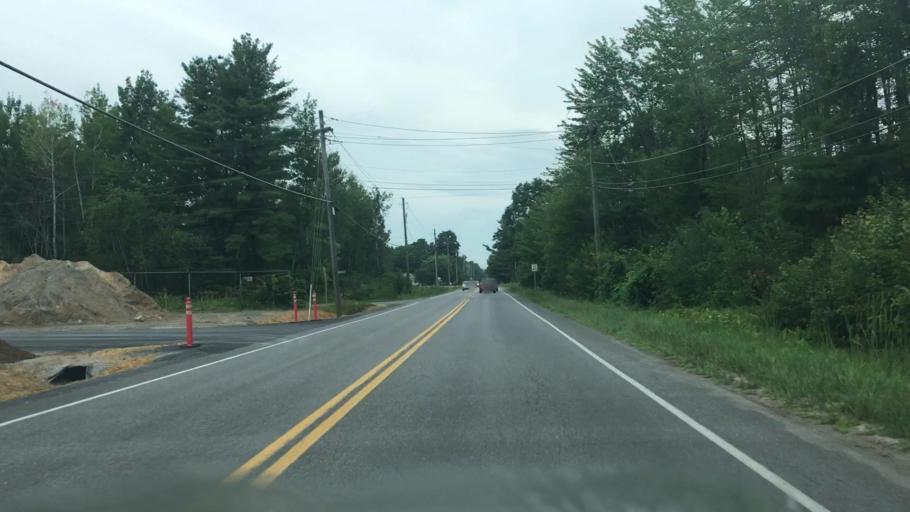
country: US
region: New York
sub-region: Clinton County
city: Plattsburgh West
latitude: 44.6615
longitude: -73.5092
